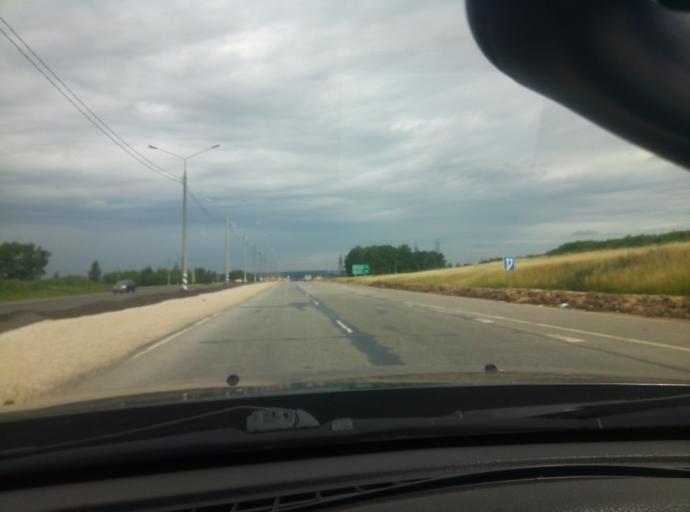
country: RU
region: Tula
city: Novogurovskiy
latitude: 54.4709
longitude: 37.5117
